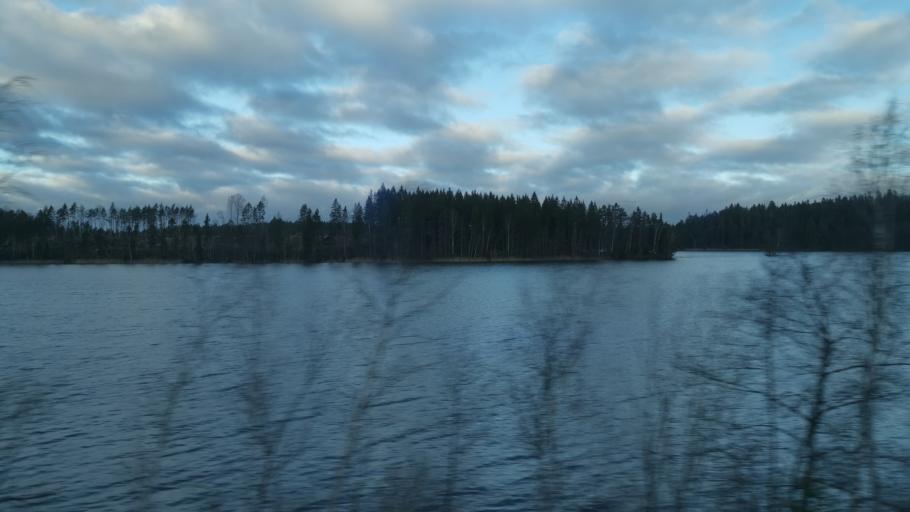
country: SE
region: Soedermanland
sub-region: Flens Kommun
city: Flen
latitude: 59.0418
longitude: 16.5368
